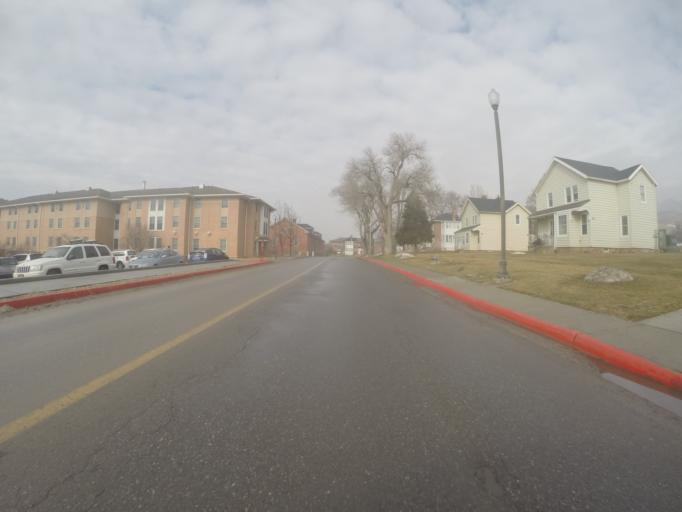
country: US
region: Utah
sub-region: Salt Lake County
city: Canyon Rim
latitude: 40.7639
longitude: -111.8295
